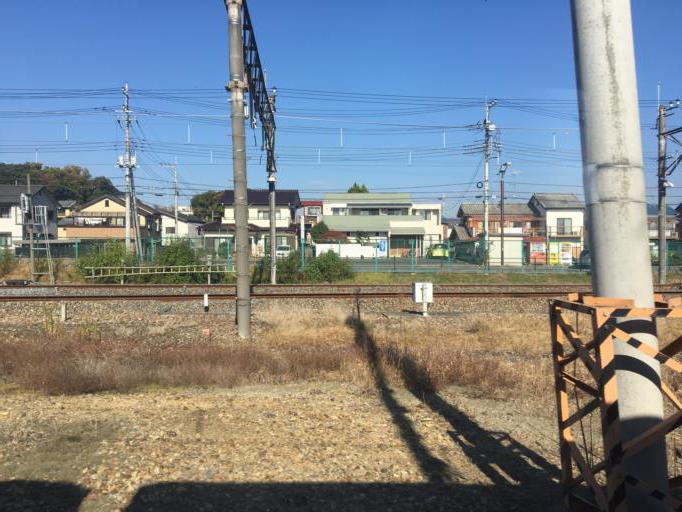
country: JP
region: Tochigi
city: Sano
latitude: 36.3168
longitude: 139.5810
